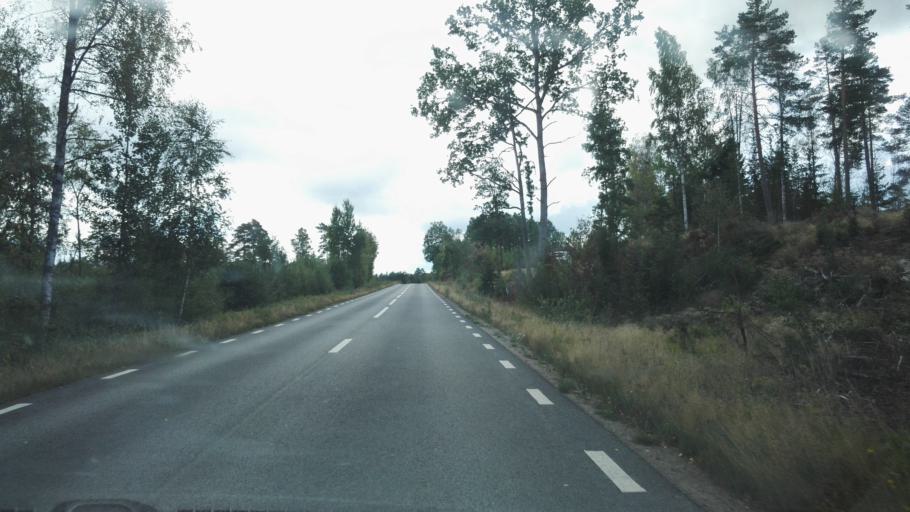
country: SE
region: Kronoberg
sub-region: Vaxjo Kommun
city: Braas
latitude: 57.1417
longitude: 14.9625
